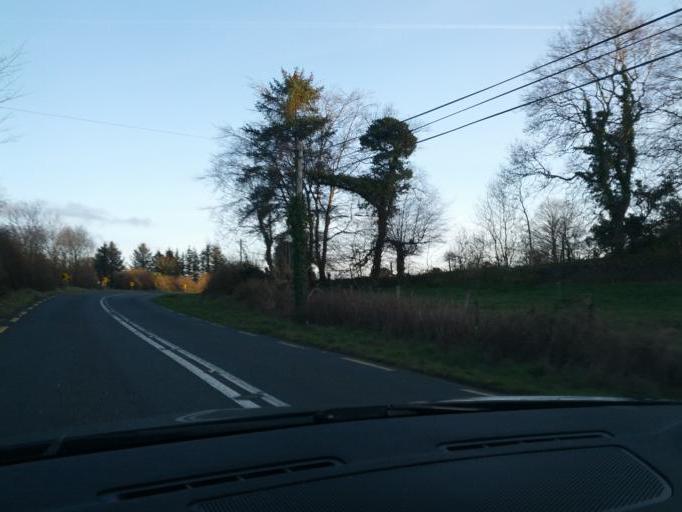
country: IE
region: Connaught
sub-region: Sligo
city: Tobercurry
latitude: 54.0822
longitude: -8.7034
